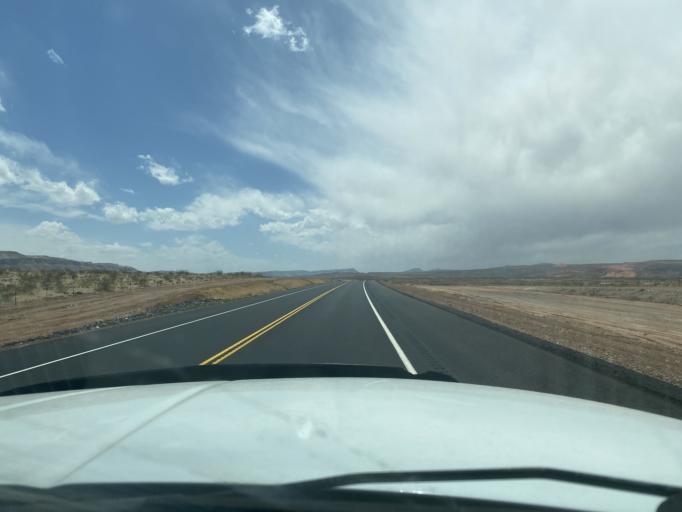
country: US
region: Utah
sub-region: Washington County
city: Hurricane
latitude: 37.1497
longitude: -113.3458
